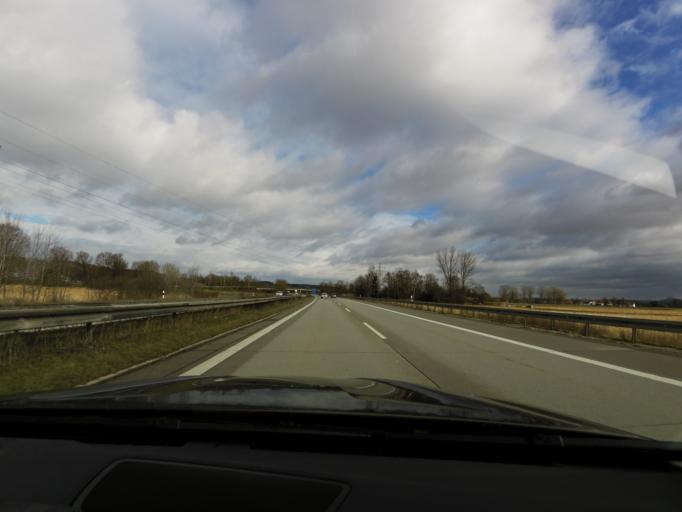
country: DE
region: Bavaria
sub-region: Lower Bavaria
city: Eching
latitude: 48.5218
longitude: 12.0658
